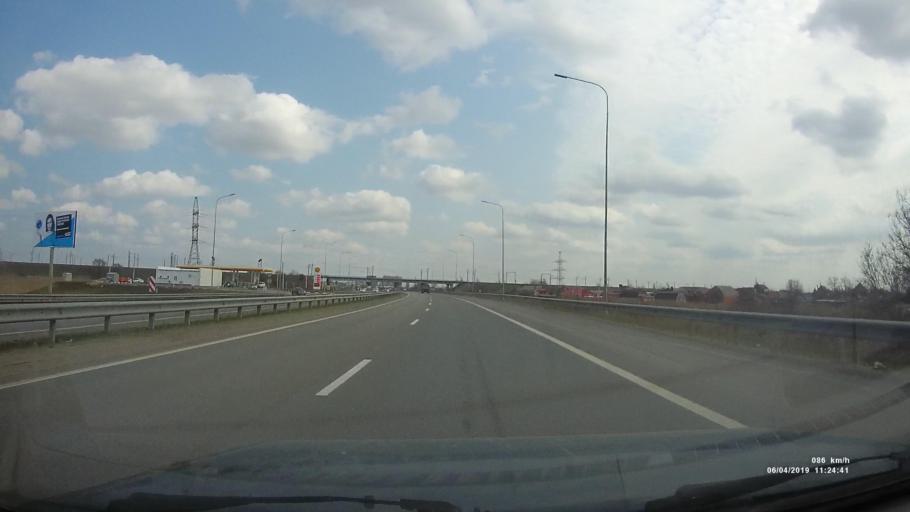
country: RU
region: Rostov
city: Bataysk
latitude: 47.1419
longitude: 39.6950
